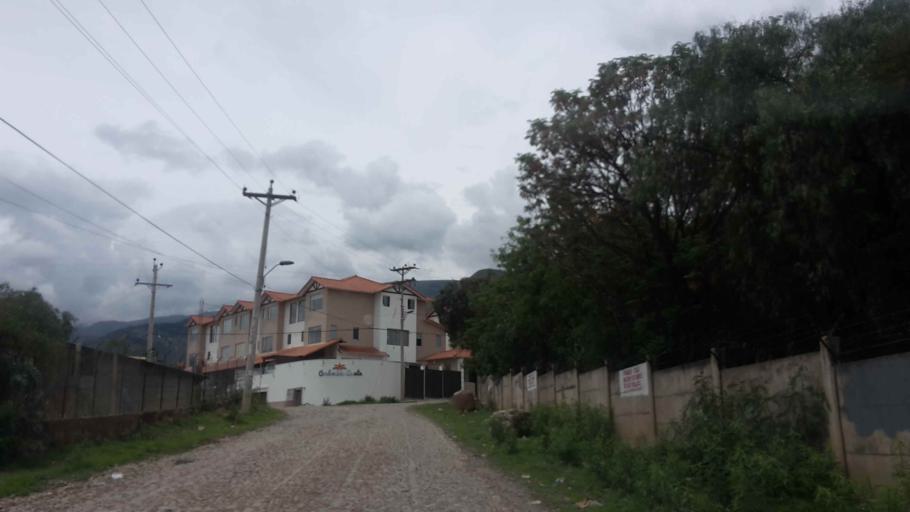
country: BO
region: Cochabamba
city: Cochabamba
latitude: -17.3404
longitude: -66.1880
